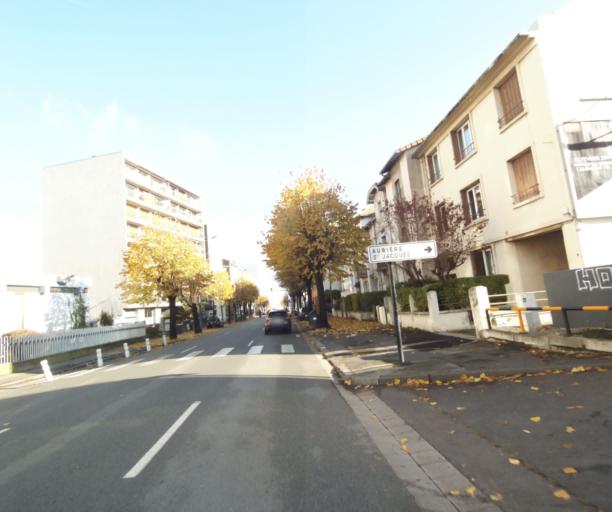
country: FR
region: Auvergne
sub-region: Departement du Puy-de-Dome
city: Clermont-Ferrand
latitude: 45.7711
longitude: 3.0930
